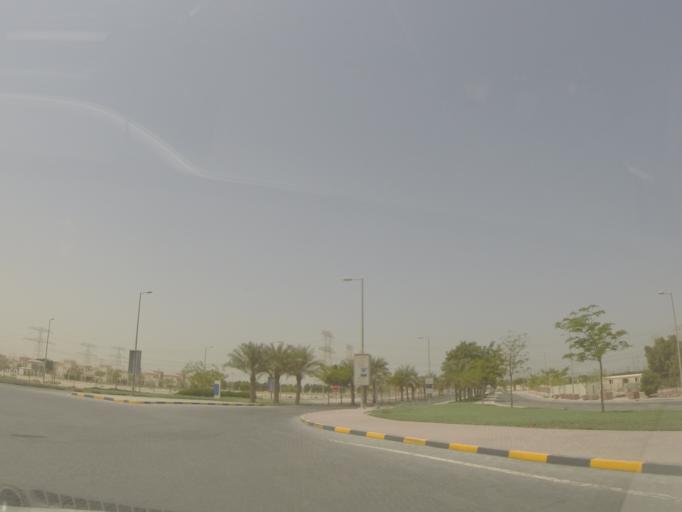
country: AE
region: Dubai
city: Dubai
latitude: 25.0367
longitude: 55.1761
